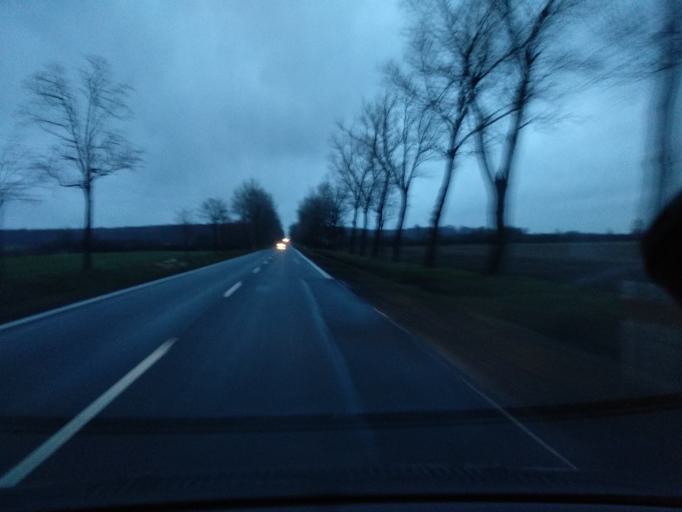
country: PL
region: Lower Silesian Voivodeship
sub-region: Powiat legnicki
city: Prochowice
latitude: 51.2401
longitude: 16.4146
